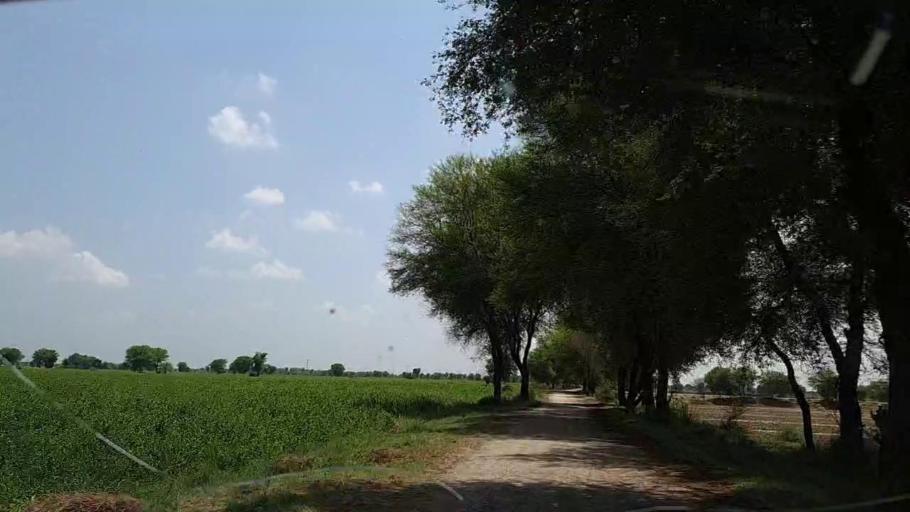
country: PK
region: Sindh
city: Tharu Shah
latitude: 27.0135
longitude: 68.0685
